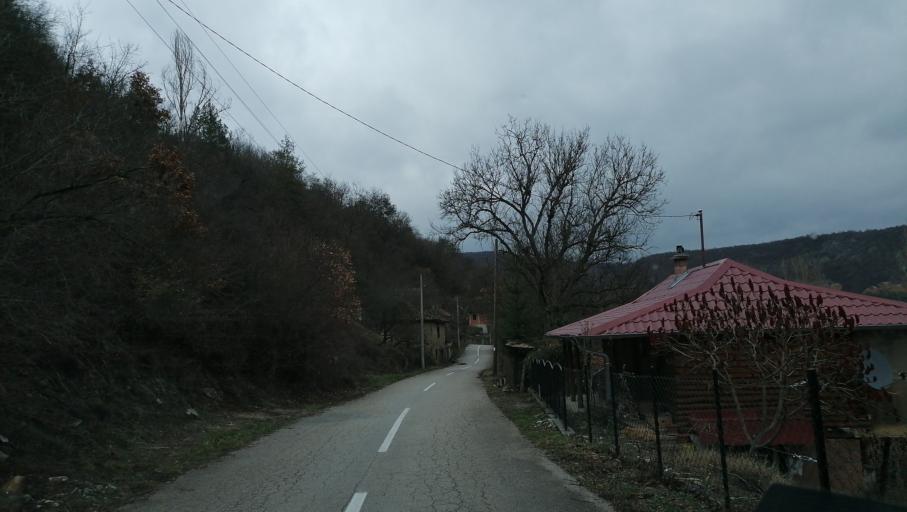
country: RS
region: Central Serbia
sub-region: Pirotski Okrug
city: Dimitrovgrad
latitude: 42.9271
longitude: 22.7698
